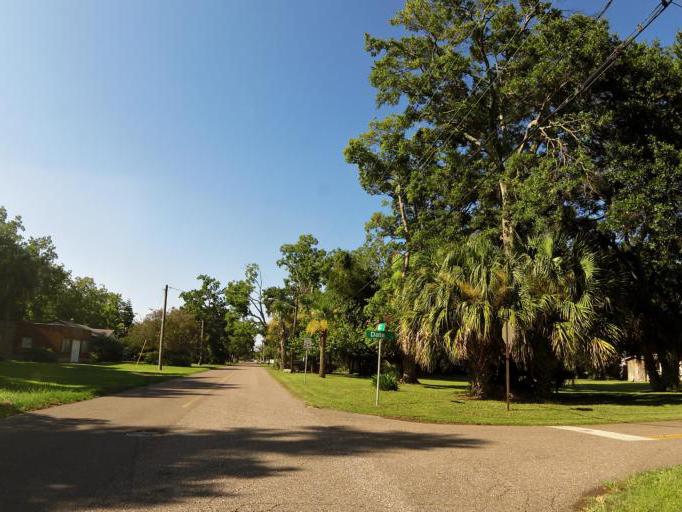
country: US
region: Florida
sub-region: Nassau County
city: Fernandina Beach
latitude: 30.6660
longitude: -81.4637
